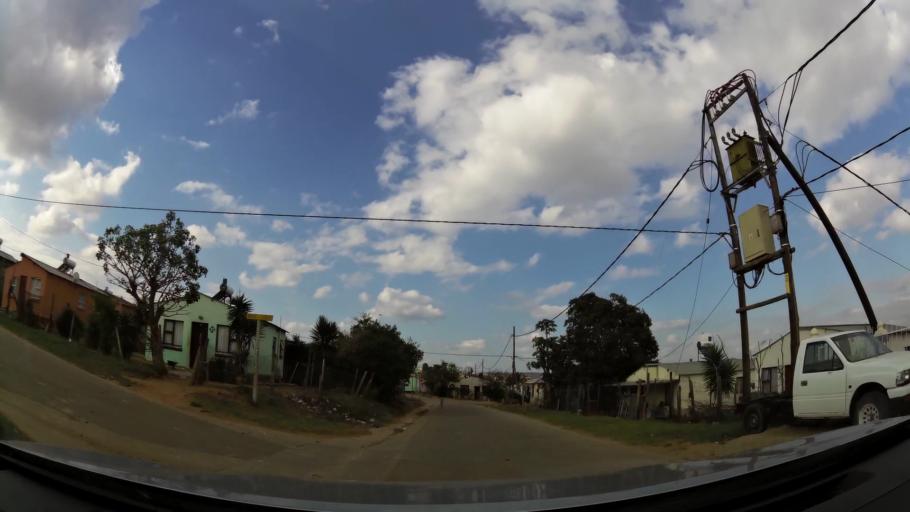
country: ZA
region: Eastern Cape
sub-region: Nelson Mandela Bay Metropolitan Municipality
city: Uitenhage
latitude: -33.7306
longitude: 25.3929
